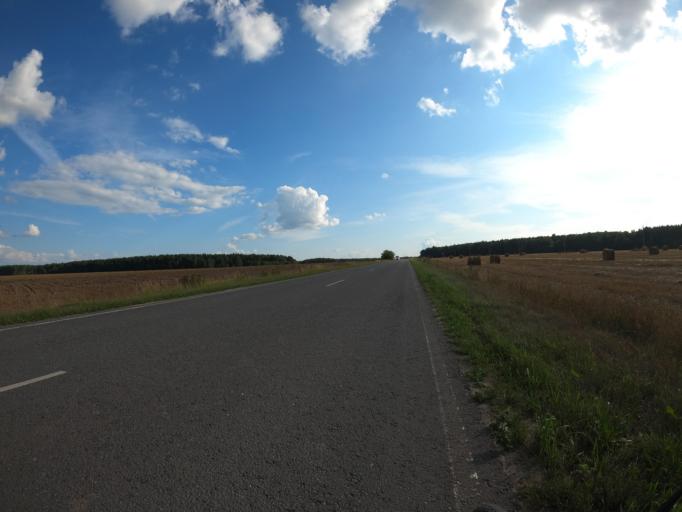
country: RU
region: Moskovskaya
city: Meshcherino
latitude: 55.1756
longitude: 38.4691
